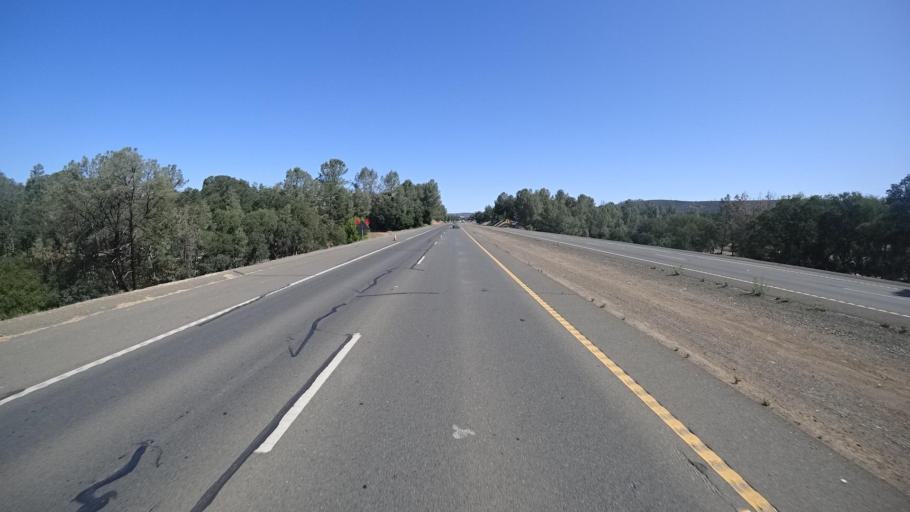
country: US
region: California
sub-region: Lake County
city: Clearlake
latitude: 38.9458
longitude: -122.6235
